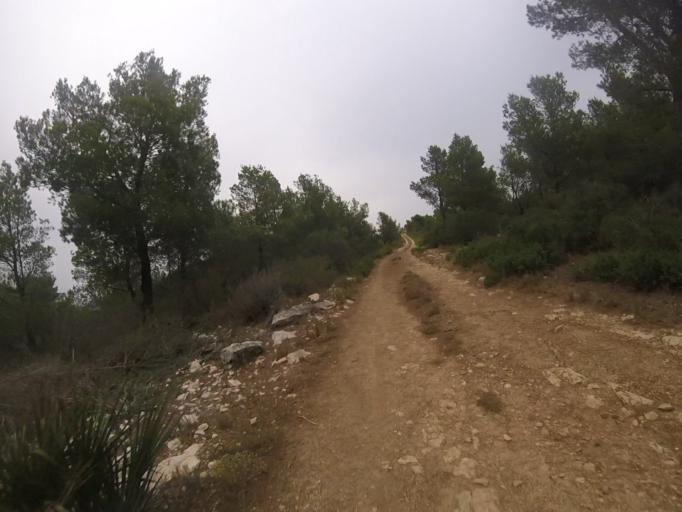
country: ES
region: Valencia
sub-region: Provincia de Castello
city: Alcoceber
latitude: 40.2831
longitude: 0.2838
